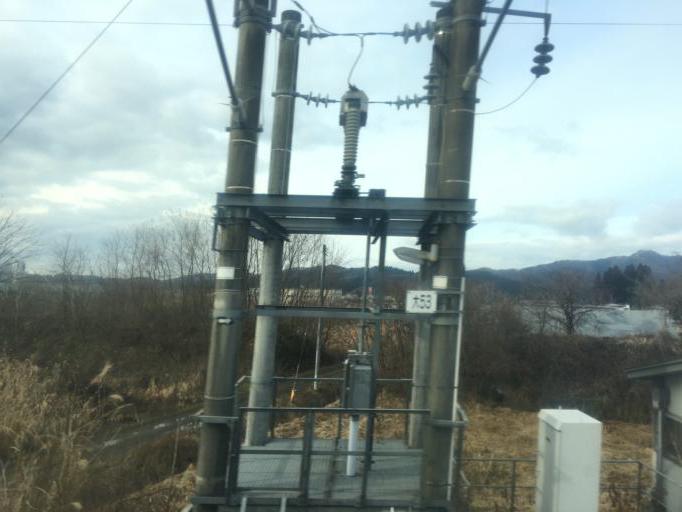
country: JP
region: Akita
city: Odate
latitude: 40.2970
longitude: 140.5662
